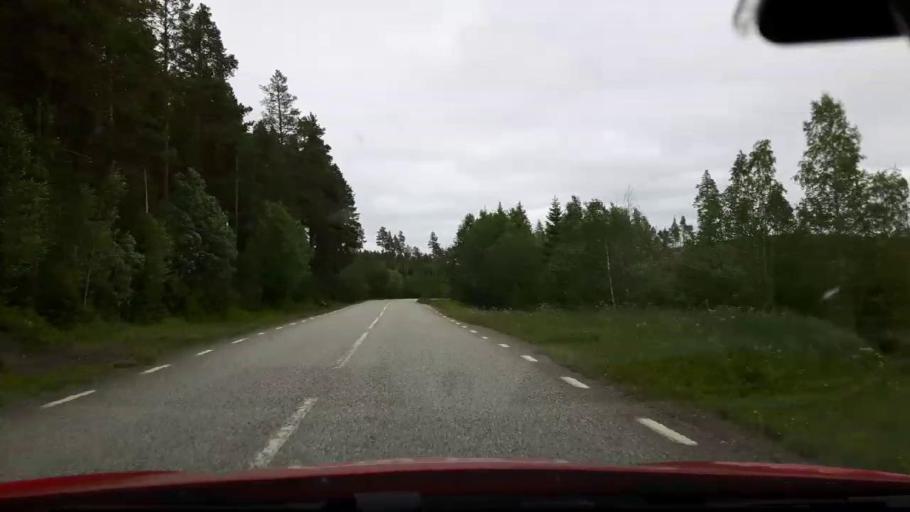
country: SE
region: Jaemtland
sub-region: Stroemsunds Kommun
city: Stroemsund
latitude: 63.3438
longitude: 15.7502
